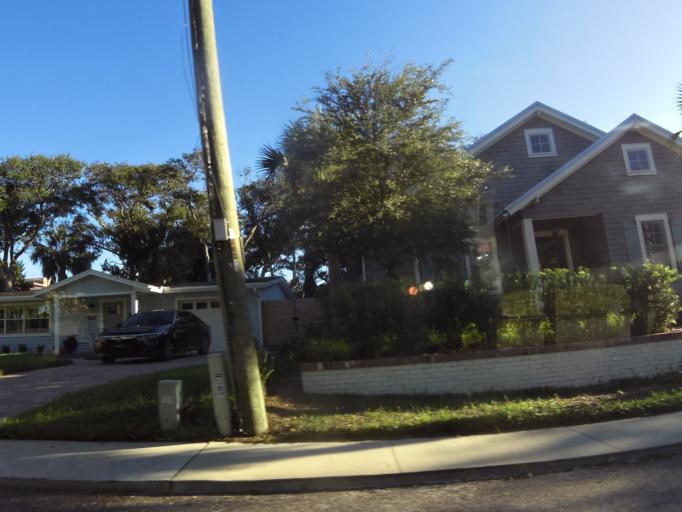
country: US
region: Florida
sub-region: Duval County
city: Atlantic Beach
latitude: 30.3261
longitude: -81.3991
